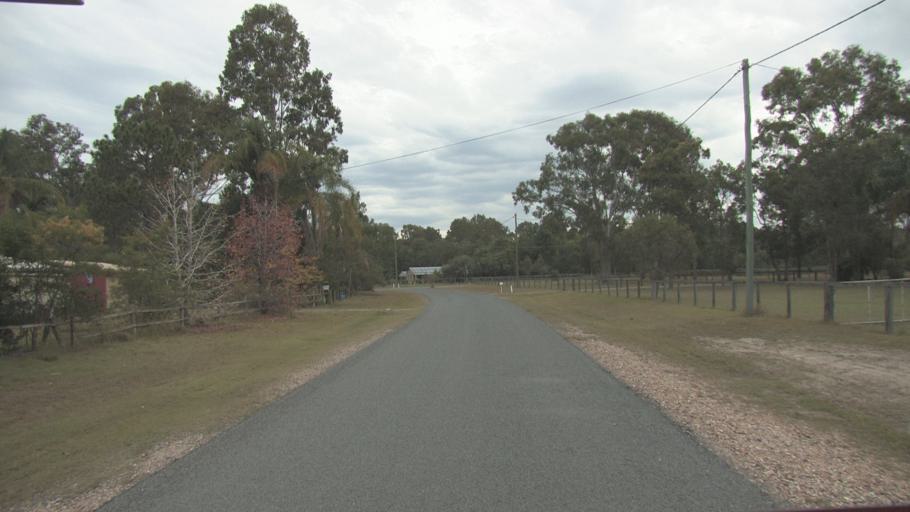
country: AU
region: Queensland
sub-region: Logan
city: Chambers Flat
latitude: -27.7998
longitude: 153.1255
